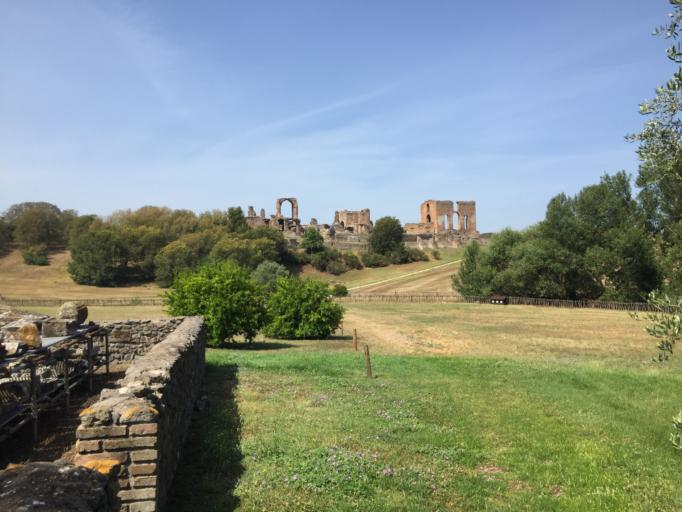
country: IT
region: Latium
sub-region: Citta metropolitana di Roma Capitale
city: Ciampino
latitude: 41.8312
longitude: 12.5541
